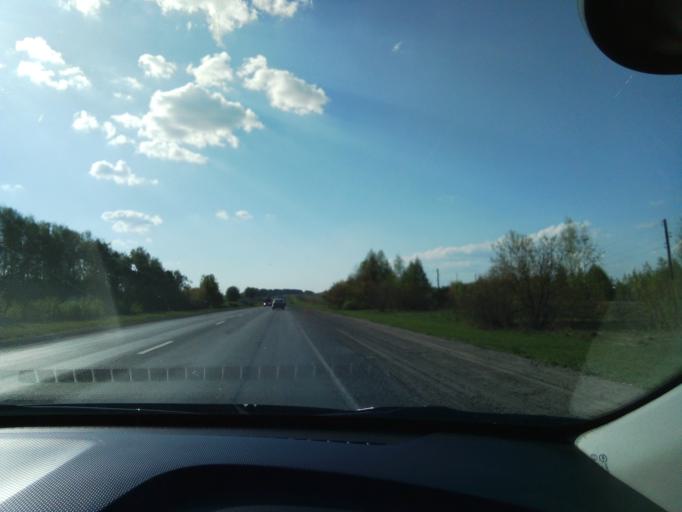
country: RU
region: Chuvashia
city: Kugesi
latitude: 56.0586
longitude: 47.2597
